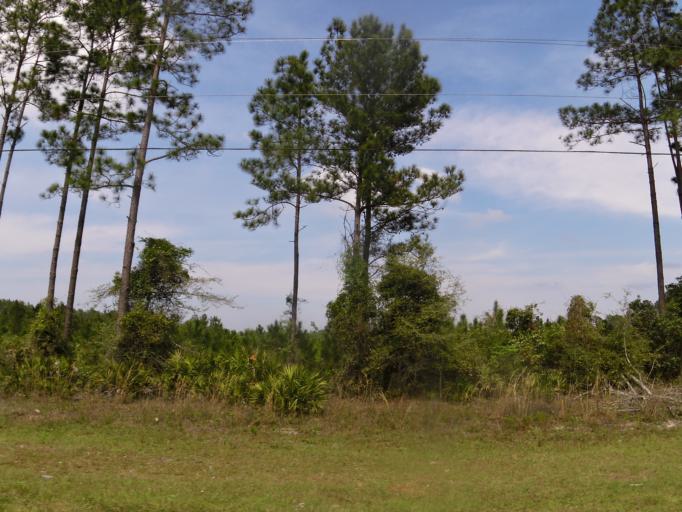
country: US
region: Georgia
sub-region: Camden County
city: Kingsland
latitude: 30.7756
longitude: -81.6775
